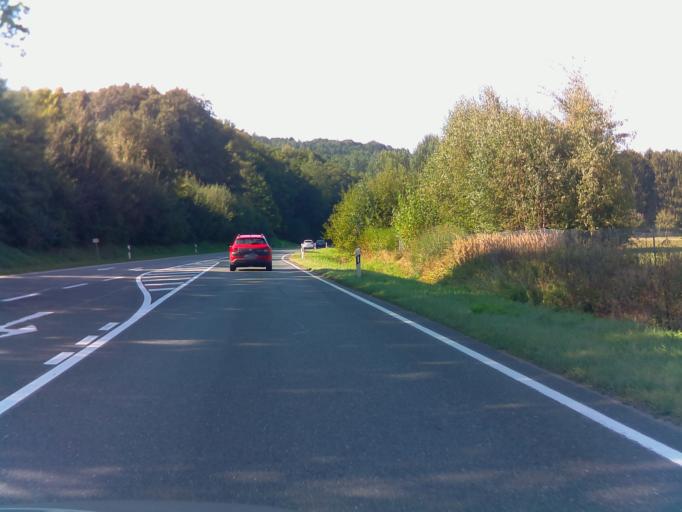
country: DE
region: Bavaria
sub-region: Upper Franconia
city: Michelau
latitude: 50.1489
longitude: 11.1325
